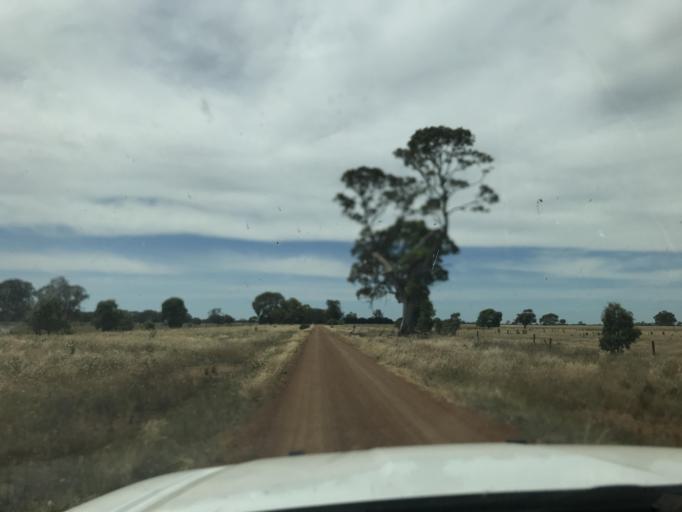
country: AU
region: South Australia
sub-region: Wattle Range
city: Penola
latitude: -37.0230
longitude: 141.4868
